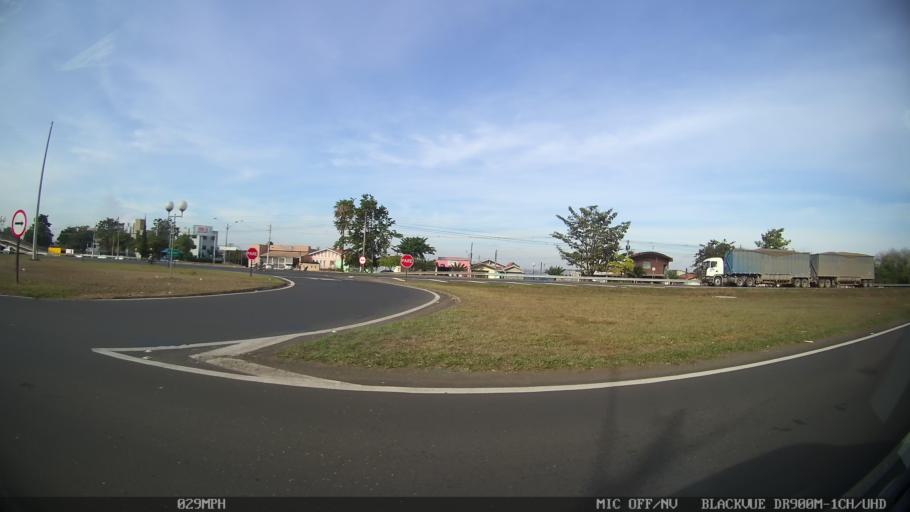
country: BR
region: Sao Paulo
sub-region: Piracicaba
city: Piracicaba
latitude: -22.6799
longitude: -47.7037
